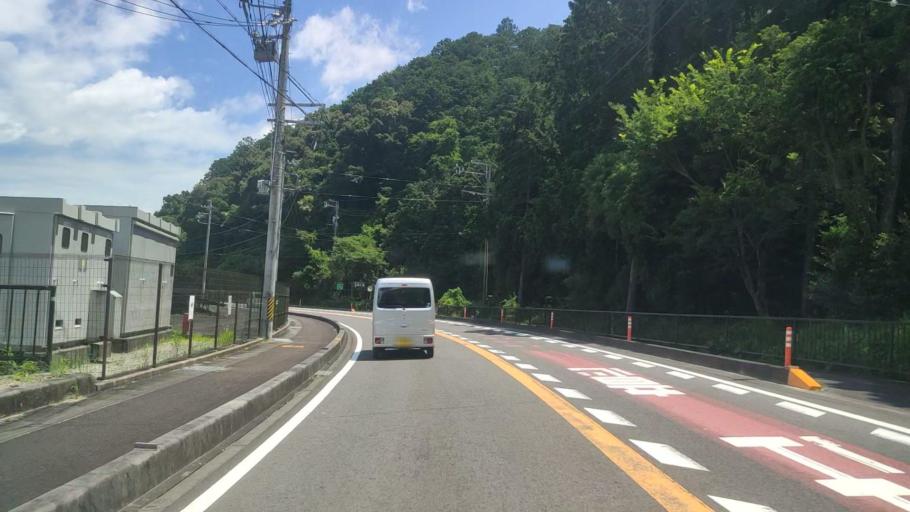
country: JP
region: Mie
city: Owase
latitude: 34.1152
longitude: 136.2203
